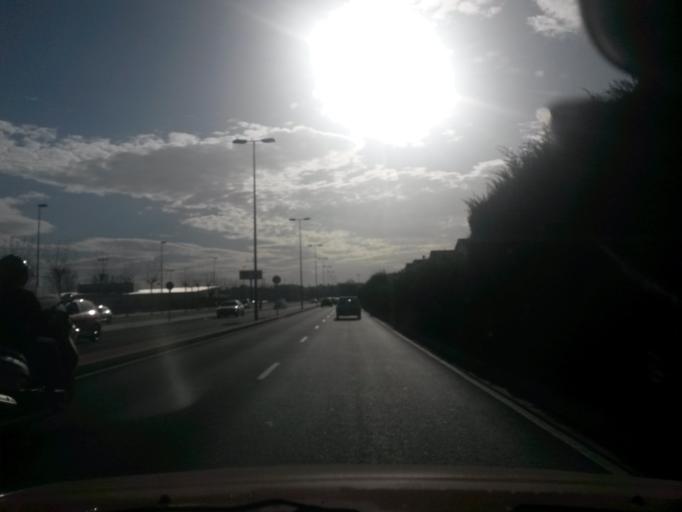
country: ES
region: Castille and Leon
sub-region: Provincia de Salamanca
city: Santa Marta de Tormes
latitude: 40.9557
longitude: -5.6431
